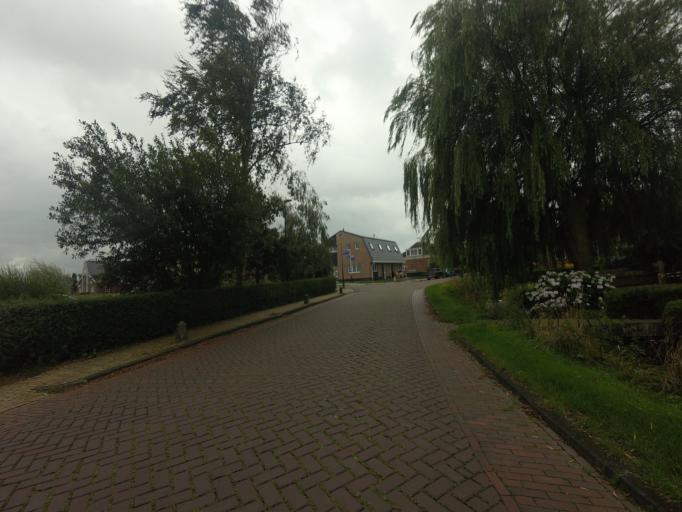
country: NL
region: Friesland
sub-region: Sudwest Fryslan
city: Heeg
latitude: 52.9954
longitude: 5.5487
